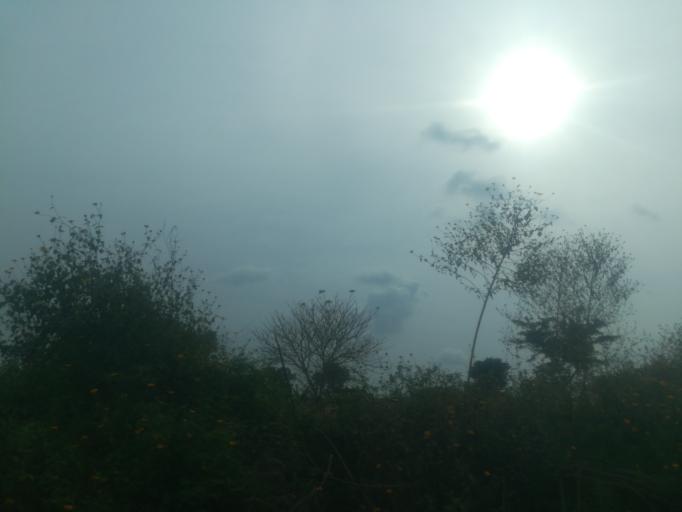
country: NG
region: Ogun
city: Ayetoro
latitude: 7.2867
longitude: 3.0851
